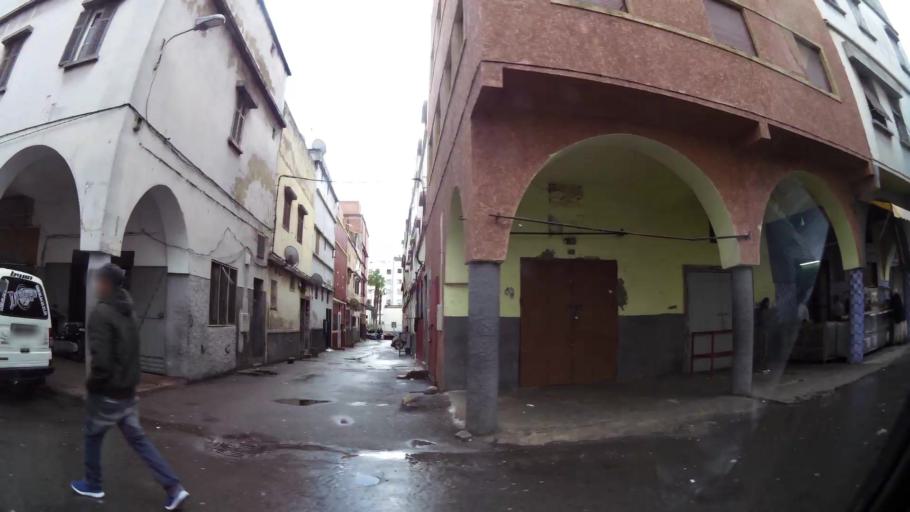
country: MA
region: Grand Casablanca
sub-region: Casablanca
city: Casablanca
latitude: 33.5664
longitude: -7.5822
